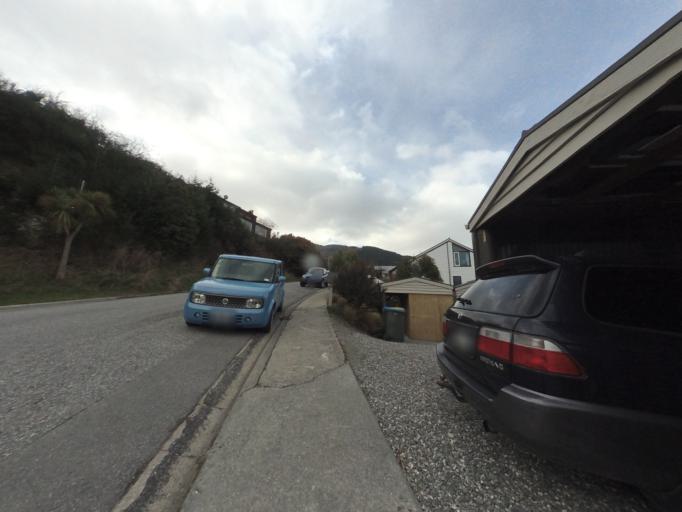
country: NZ
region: Otago
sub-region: Queenstown-Lakes District
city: Queenstown
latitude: -45.0405
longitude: 168.6334
